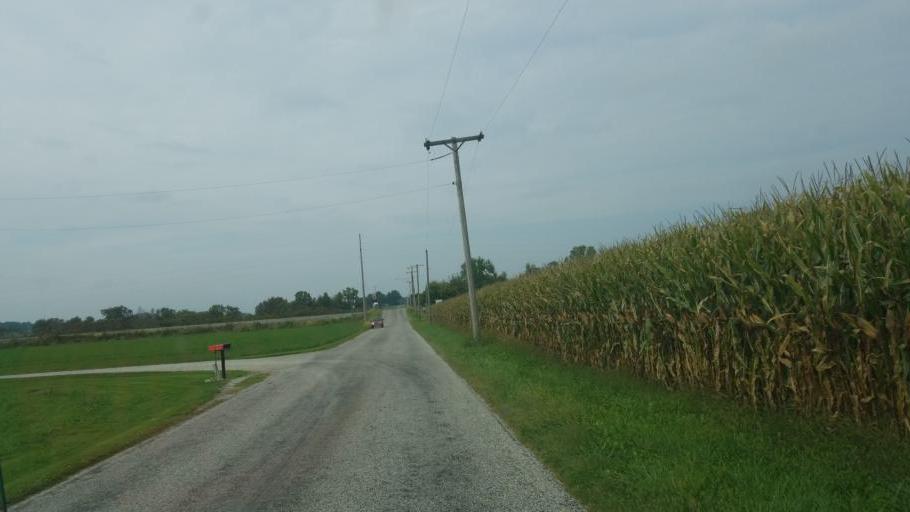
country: US
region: Ohio
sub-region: Wayne County
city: Rittman
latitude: 40.9610
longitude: -81.8123
